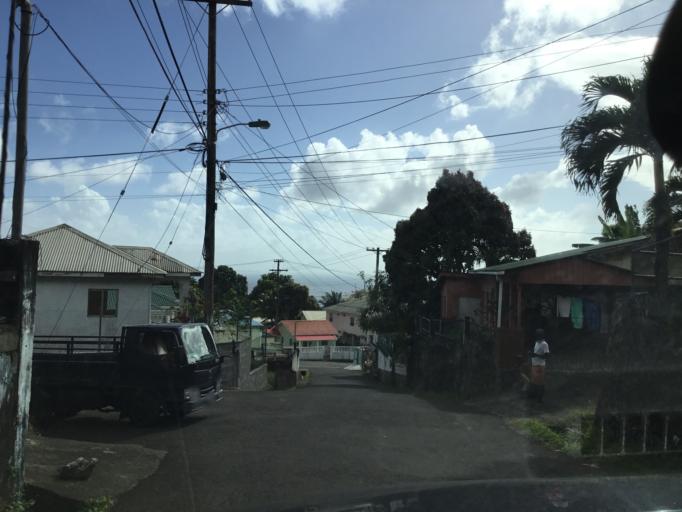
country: VC
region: Saint George
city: Kingstown
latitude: 13.1671
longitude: -61.2192
